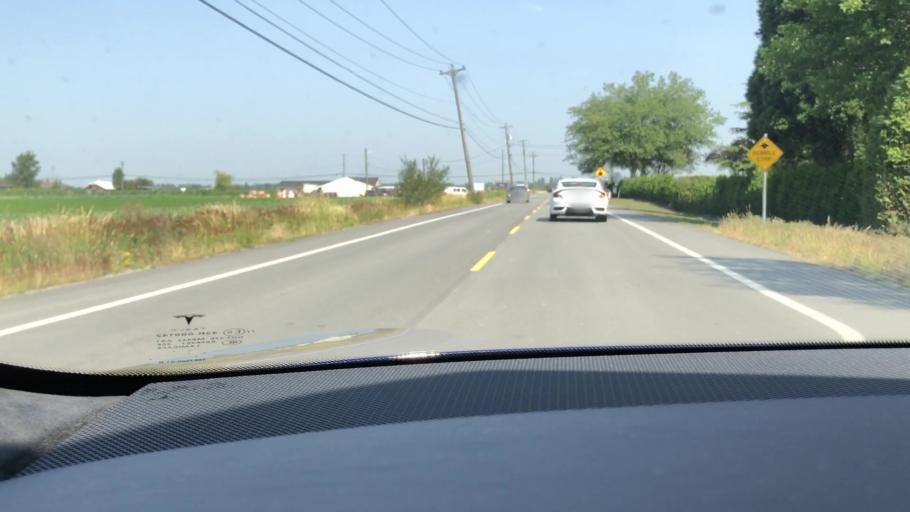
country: CA
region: British Columbia
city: Ladner
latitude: 49.0519
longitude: -123.0798
